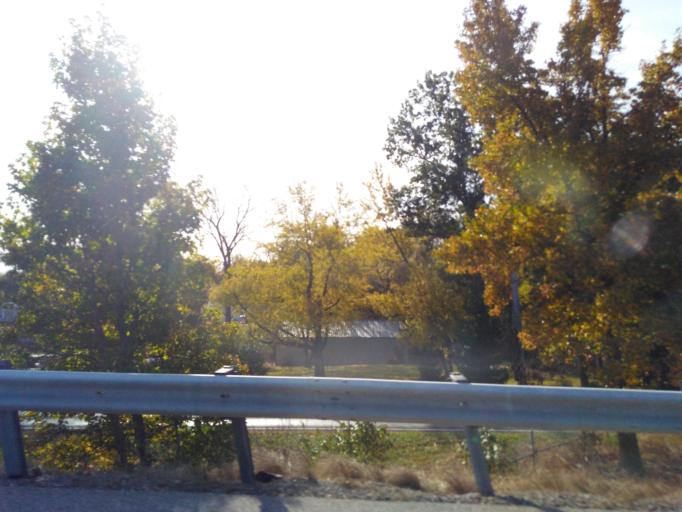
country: US
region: Illinois
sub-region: Madison County
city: Maryville
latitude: 38.7132
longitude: -89.9308
